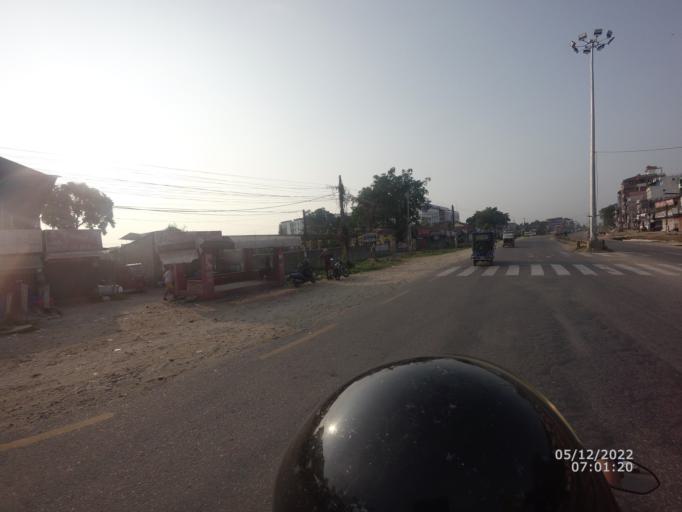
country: NP
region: Central Region
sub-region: Narayani Zone
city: Bharatpur
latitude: 27.6868
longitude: 84.4293
